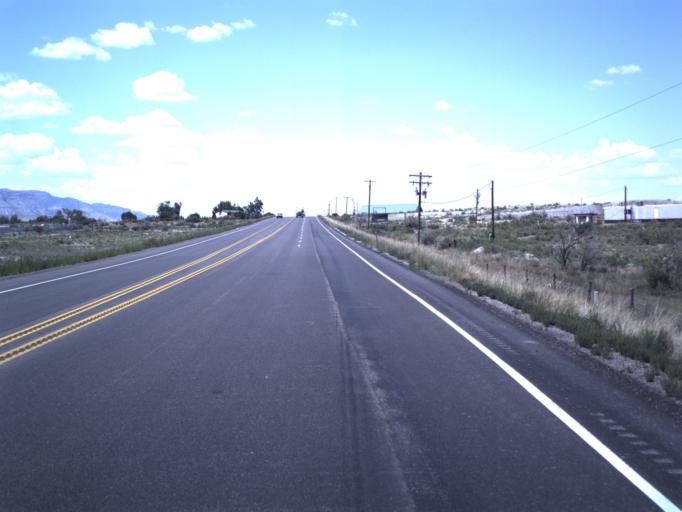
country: US
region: Utah
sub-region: Emery County
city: Huntington
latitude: 39.3133
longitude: -110.9643
